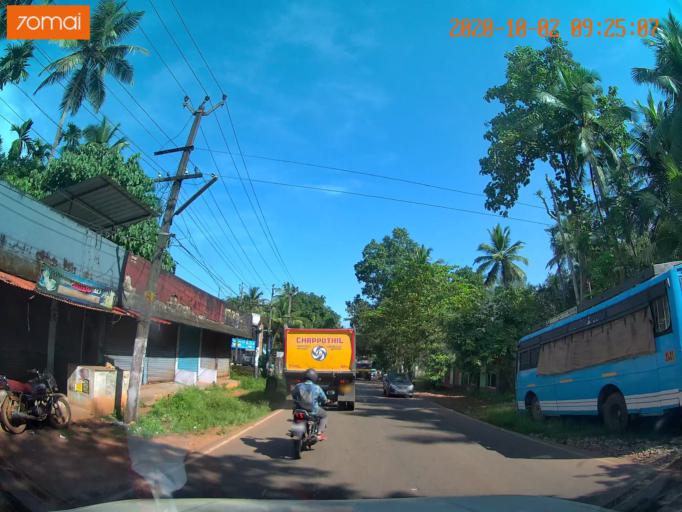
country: IN
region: Kerala
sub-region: Kozhikode
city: Naduvannur
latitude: 11.5866
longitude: 75.7658
